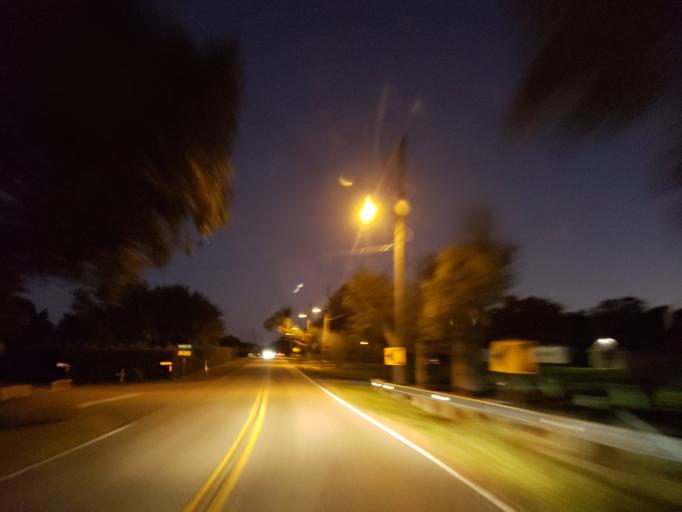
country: US
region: Florida
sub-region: Hillsborough County
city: Dover
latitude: 28.0071
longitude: -82.2240
